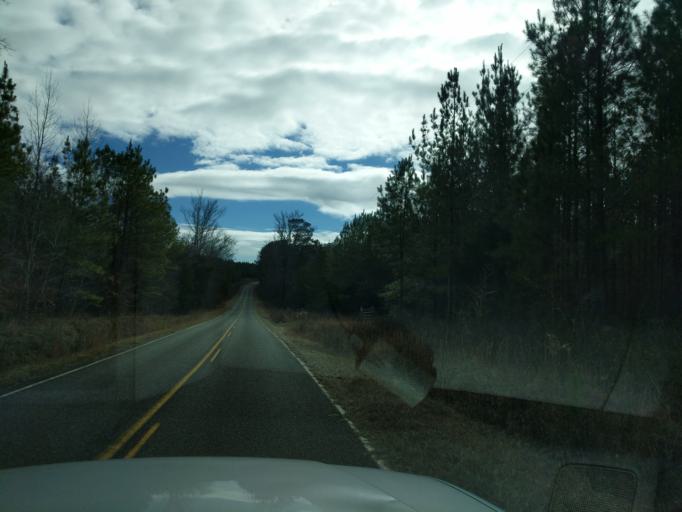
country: US
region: South Carolina
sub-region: Edgefield County
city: Edgefield
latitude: 33.9131
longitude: -82.0049
